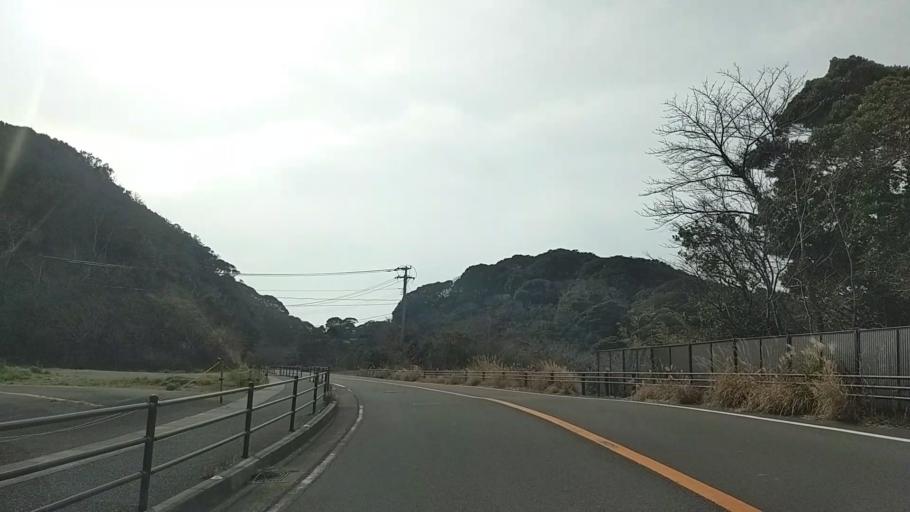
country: JP
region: Shizuoka
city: Shimoda
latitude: 34.6674
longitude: 138.9627
